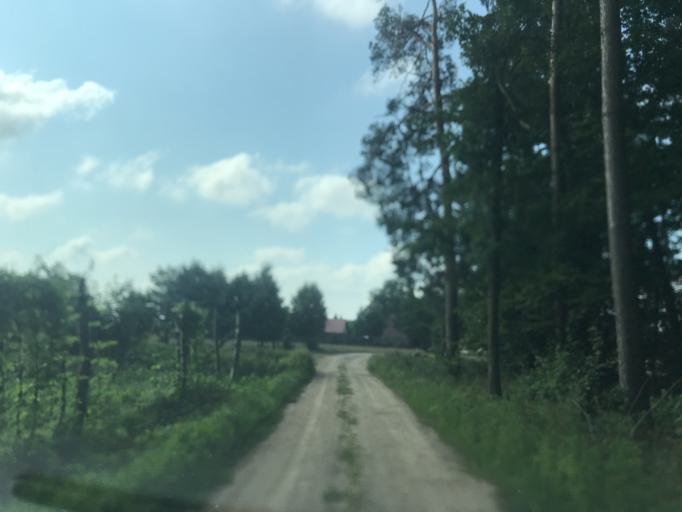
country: PL
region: Kujawsko-Pomorskie
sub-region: Powiat brodnicki
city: Brodnica
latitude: 53.3481
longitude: 19.4688
